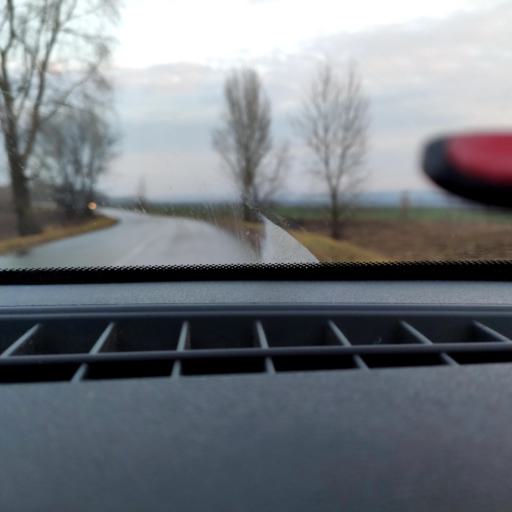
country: RU
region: Bashkortostan
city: Avdon
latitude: 54.5104
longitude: 55.8248
